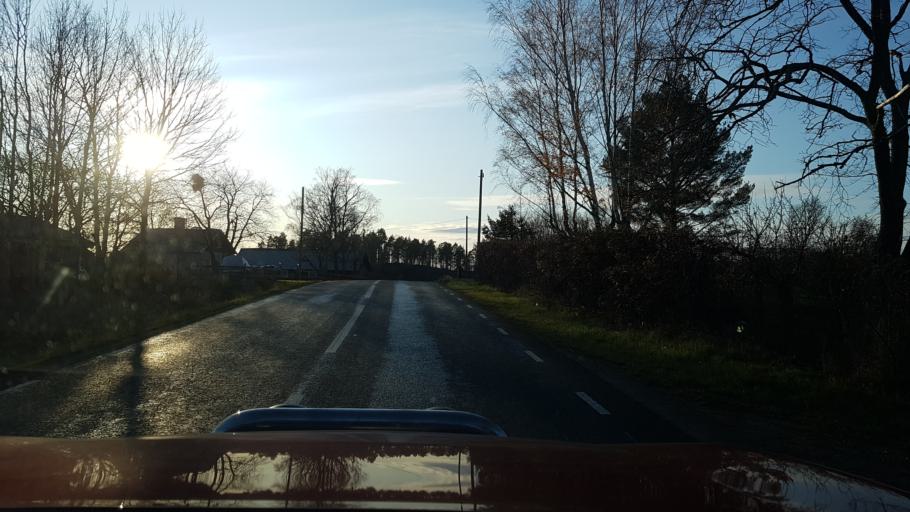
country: SE
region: OEstergoetland
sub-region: Norrkopings Kommun
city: Kimstad
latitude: 58.4832
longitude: 15.9892
